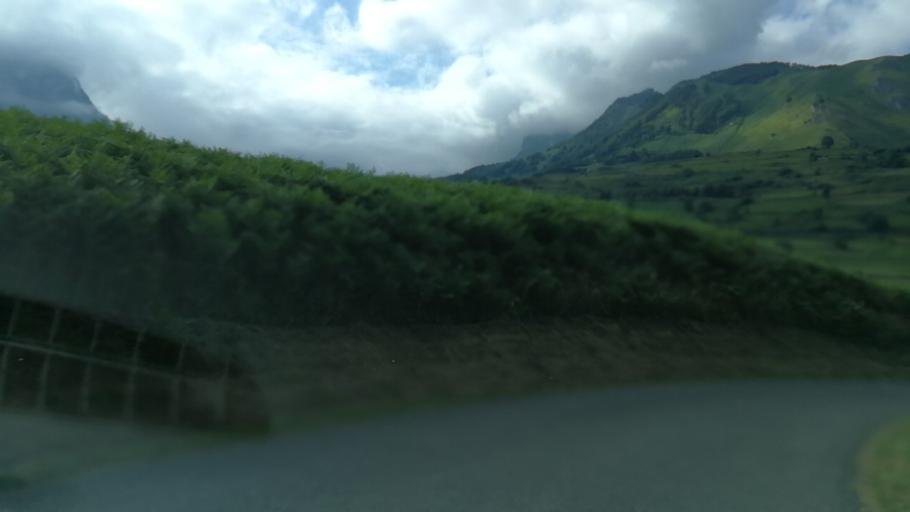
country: FR
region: Aquitaine
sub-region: Departement des Pyrenees-Atlantiques
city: Arette
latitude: 42.9258
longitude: -0.6409
